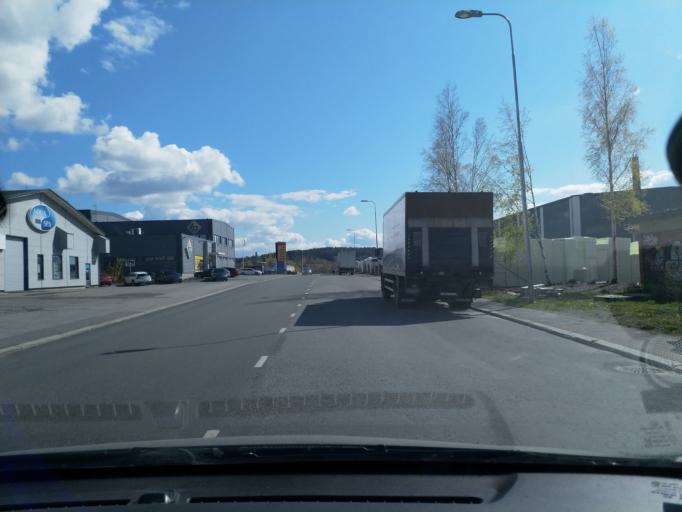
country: FI
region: Pirkanmaa
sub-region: Tampere
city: Tampere
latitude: 61.4796
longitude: 23.7896
